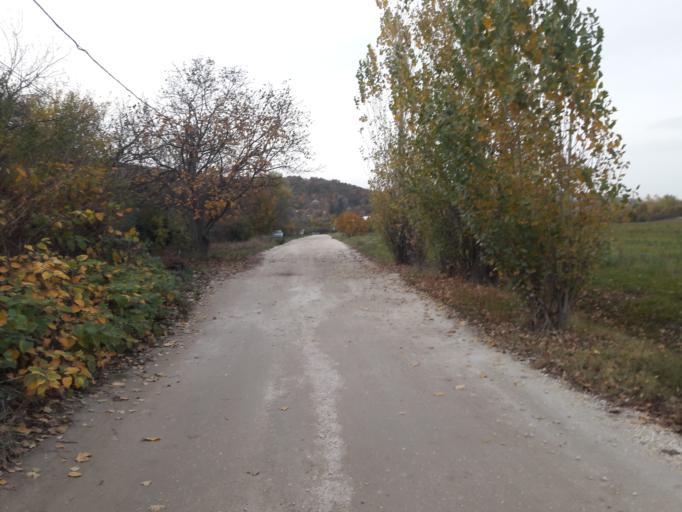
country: HU
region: Pest
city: Budaors
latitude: 47.4689
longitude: 18.9825
